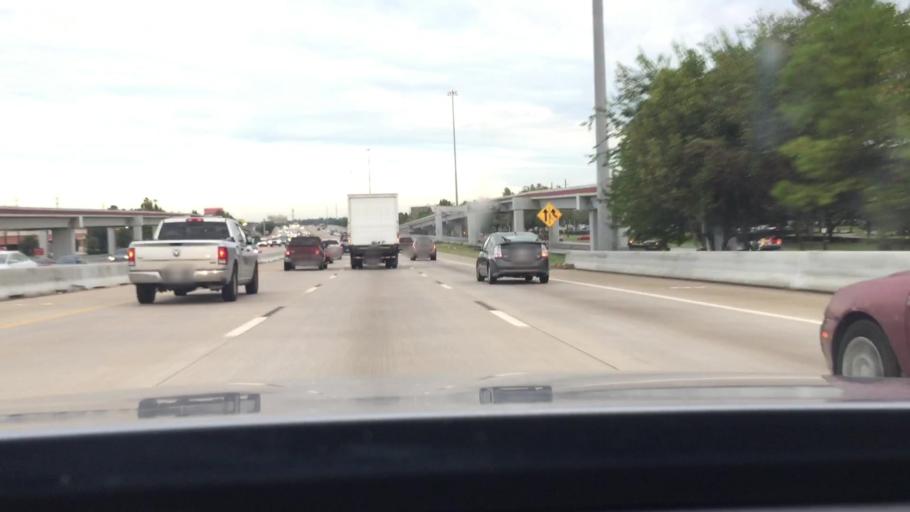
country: US
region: Texas
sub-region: Harris County
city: Jersey Village
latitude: 29.9633
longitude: -95.5495
